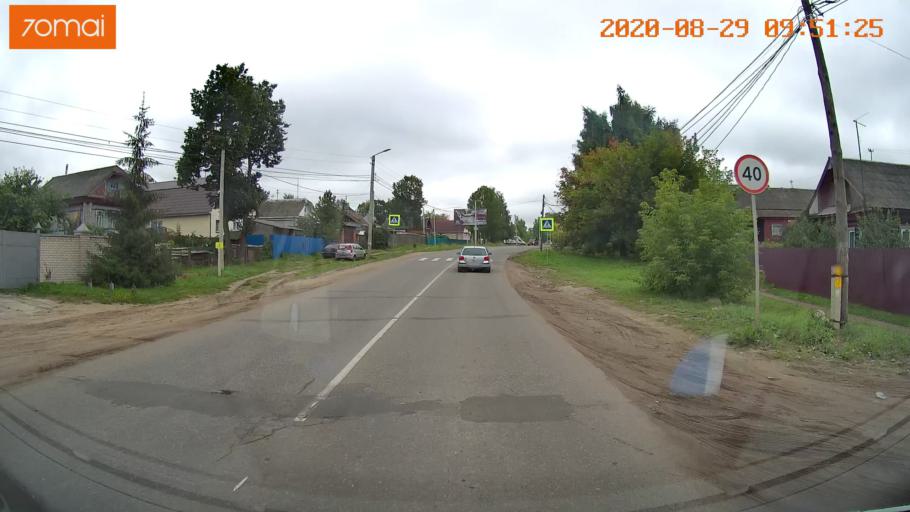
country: RU
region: Ivanovo
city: Kineshma
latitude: 57.4298
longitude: 42.1982
